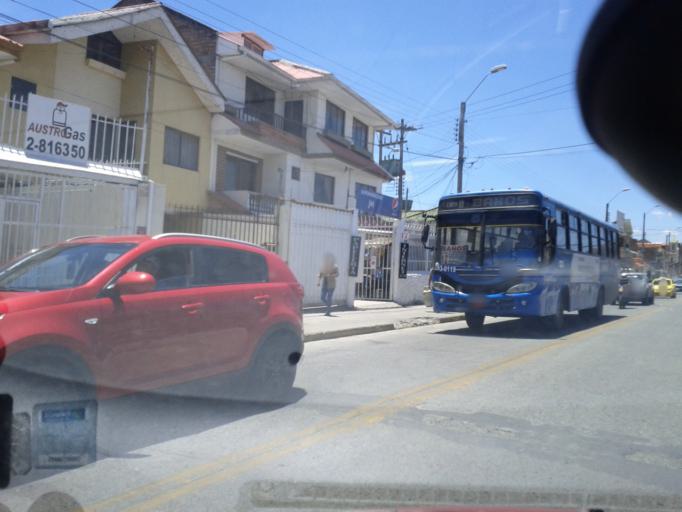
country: EC
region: Azuay
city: Cuenca
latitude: -2.9133
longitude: -79.0309
